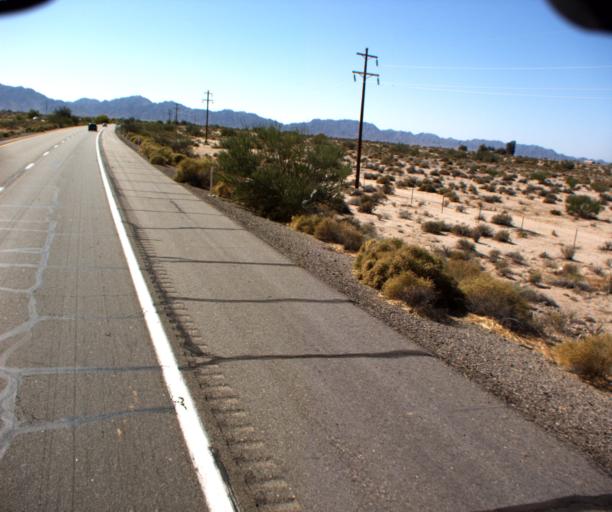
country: US
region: Arizona
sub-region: Yuma County
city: Wellton
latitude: 32.6495
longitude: -114.1956
